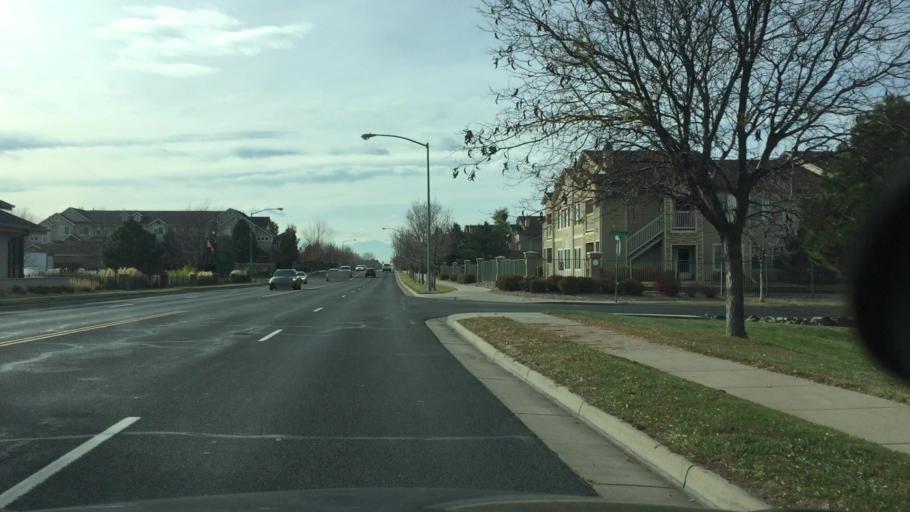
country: US
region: Colorado
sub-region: Adams County
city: Aurora
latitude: 39.6894
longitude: -104.8692
